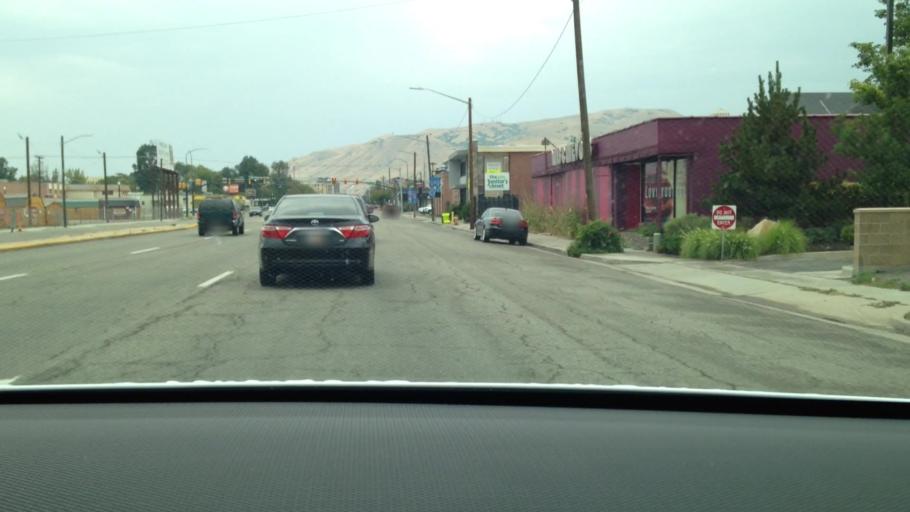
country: US
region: Utah
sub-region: Salt Lake County
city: Salt Lake City
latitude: 40.7567
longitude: -111.8995
